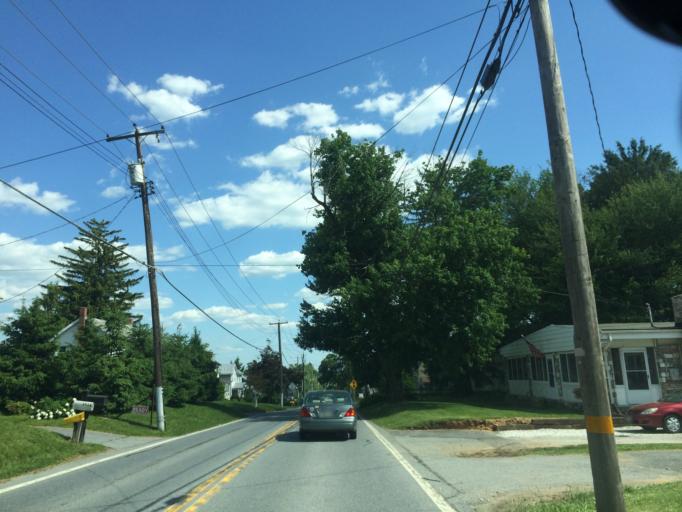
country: US
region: Maryland
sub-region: Carroll County
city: Eldersburg
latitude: 39.4665
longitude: -76.9362
